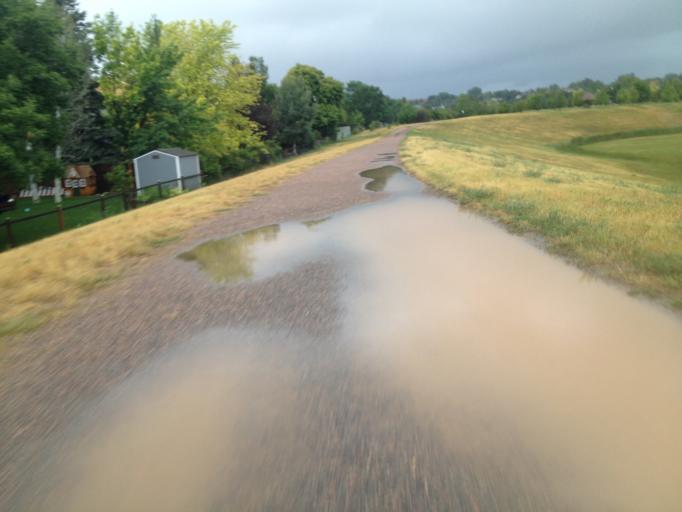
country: US
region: Colorado
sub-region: Boulder County
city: Superior
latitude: 39.9725
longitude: -105.1573
